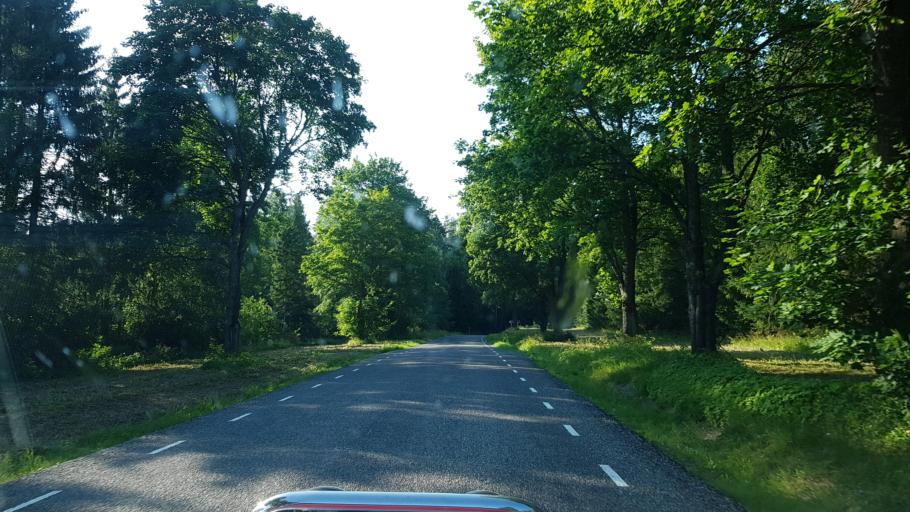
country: EE
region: Polvamaa
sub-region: Polva linn
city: Polva
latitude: 58.0113
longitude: 26.9239
